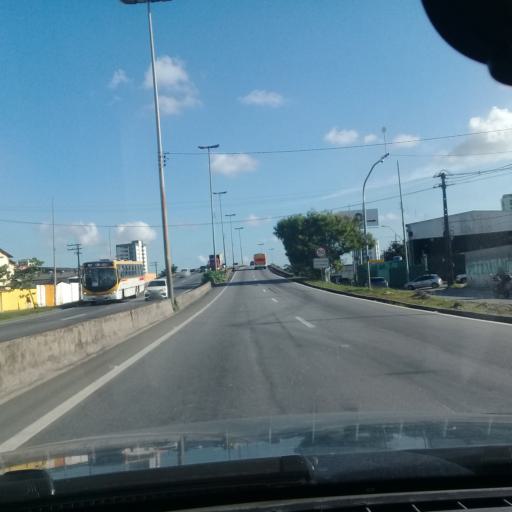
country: BR
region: Pernambuco
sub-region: Recife
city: Recife
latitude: -8.0370
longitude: -34.9416
